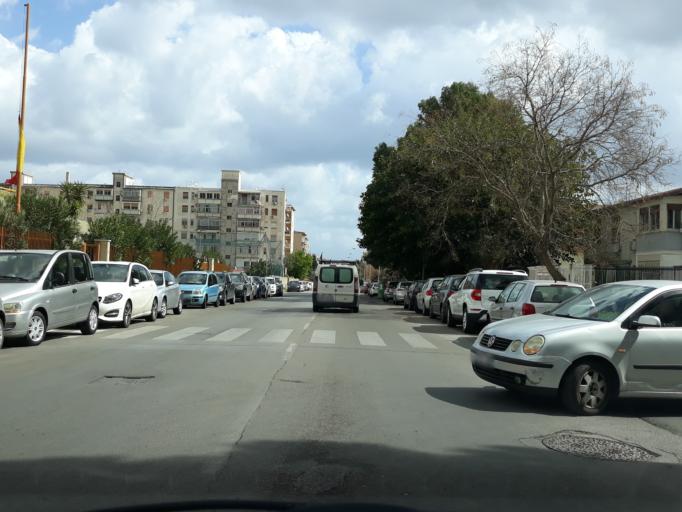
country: IT
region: Sicily
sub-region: Palermo
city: Palermo
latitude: 38.1158
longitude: 13.3347
